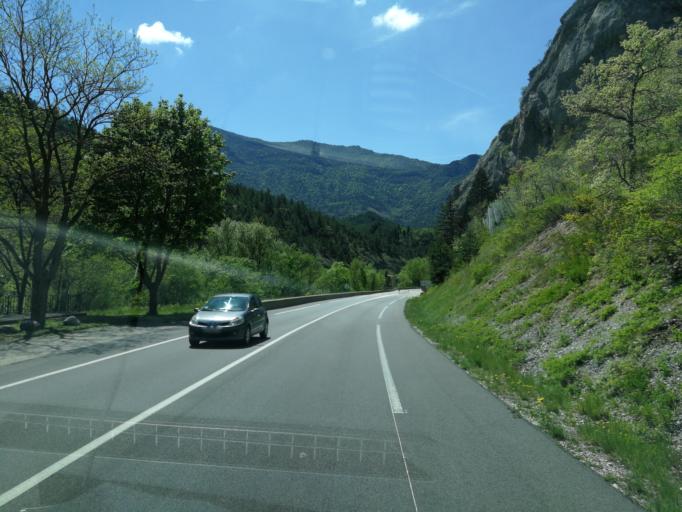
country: FR
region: Rhone-Alpes
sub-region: Departement de la Drome
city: Die
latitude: 44.6917
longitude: 5.2383
